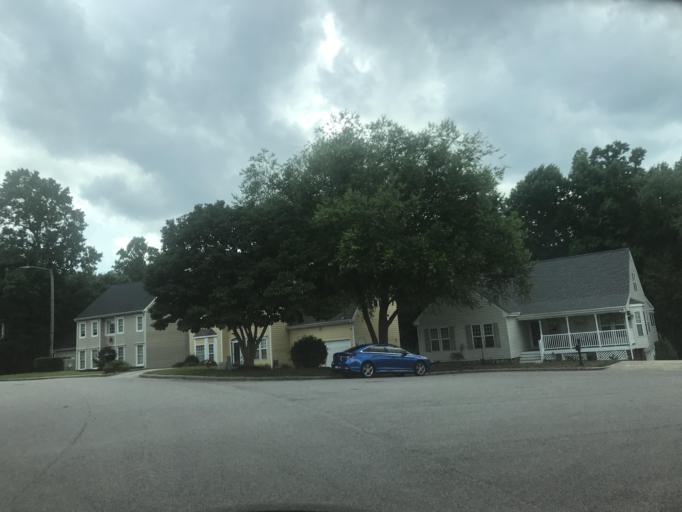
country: US
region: North Carolina
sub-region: Wake County
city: Knightdale
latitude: 35.8362
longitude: -78.5627
